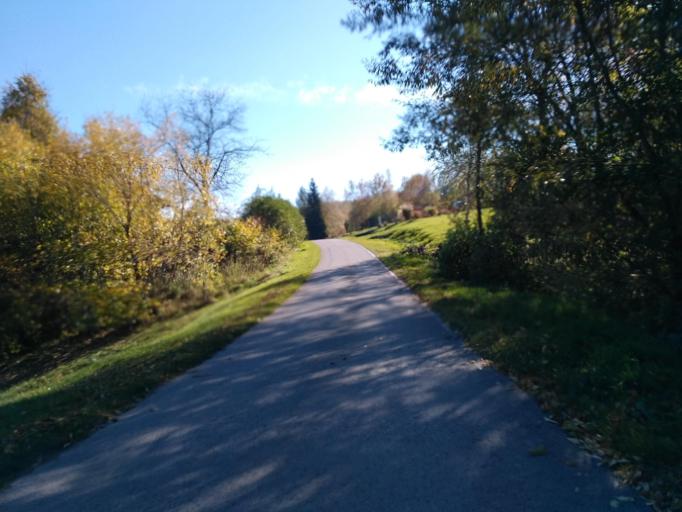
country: PL
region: Subcarpathian Voivodeship
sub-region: Powiat ropczycko-sedziszowski
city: Iwierzyce
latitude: 49.9791
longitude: 21.7277
